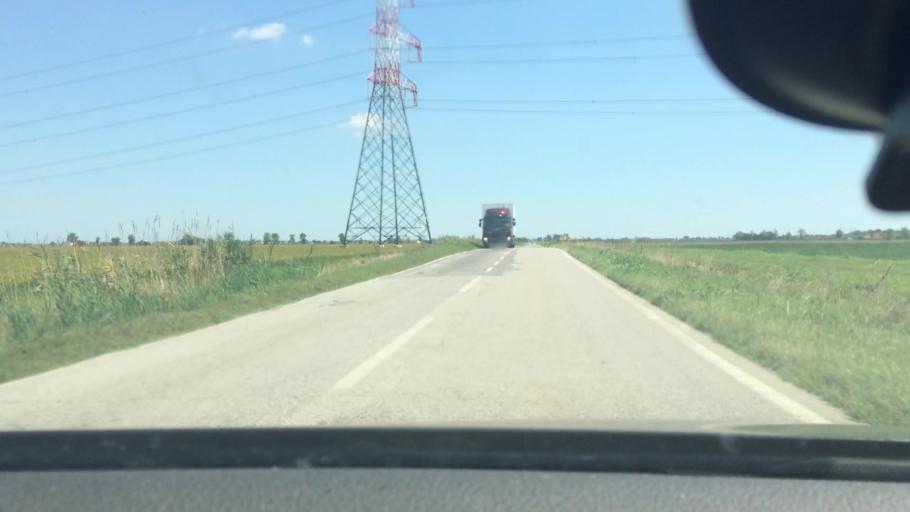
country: IT
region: Emilia-Romagna
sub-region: Provincia di Ferrara
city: Lagosanto
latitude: 44.7606
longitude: 12.0806
